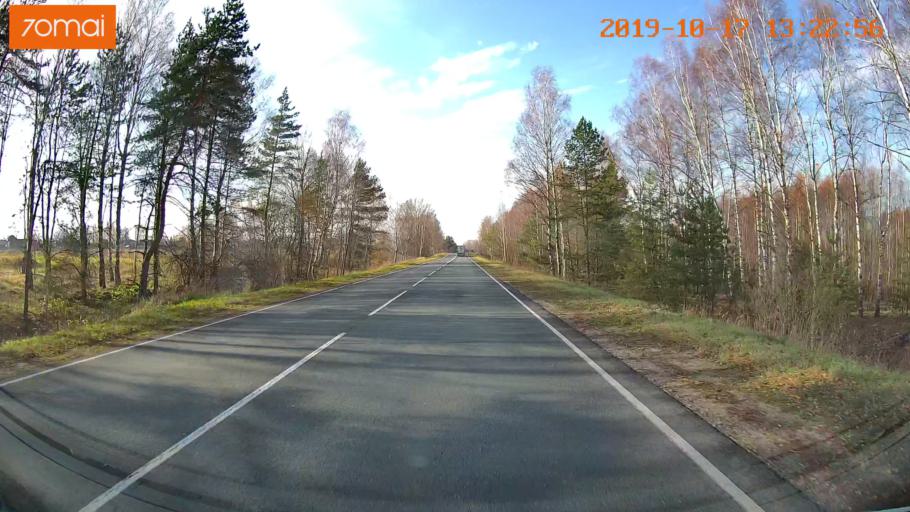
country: RU
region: Rjazan
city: Gus'-Zheleznyy
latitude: 55.0874
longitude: 40.9904
